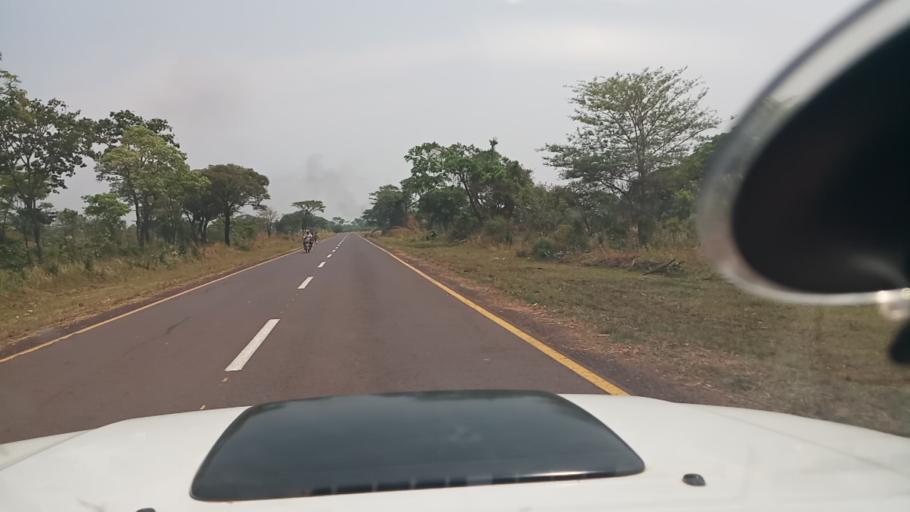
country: ZM
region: Luapula
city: Mwense
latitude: -10.7986
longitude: 28.2321
